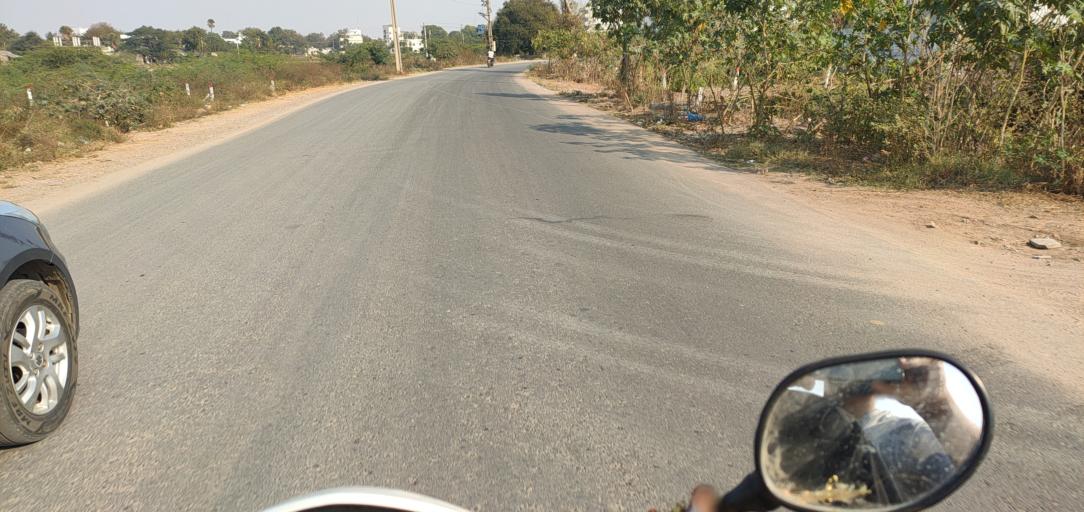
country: IN
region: Telangana
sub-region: Rangareddi
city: Lal Bahadur Nagar
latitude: 17.3422
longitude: 78.6212
